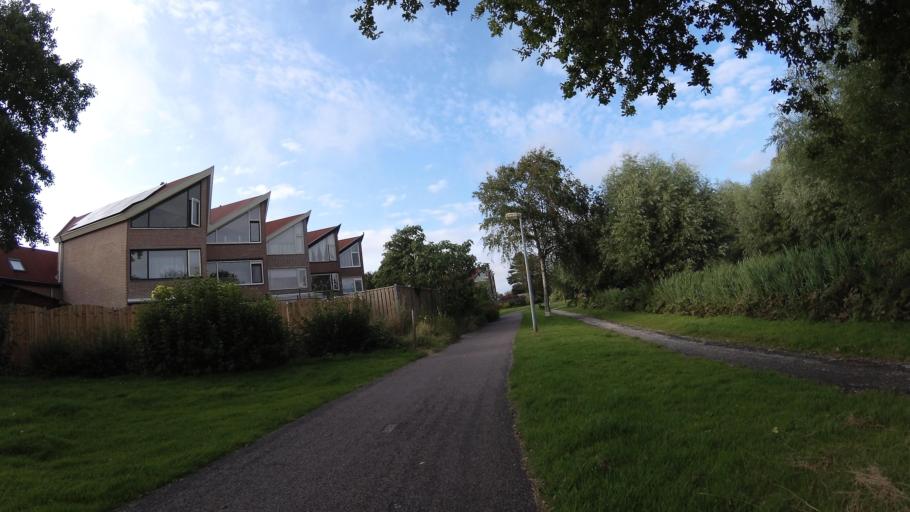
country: NL
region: North Holland
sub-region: Gemeente Den Helder
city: Den Helder
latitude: 52.8933
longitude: 4.7478
